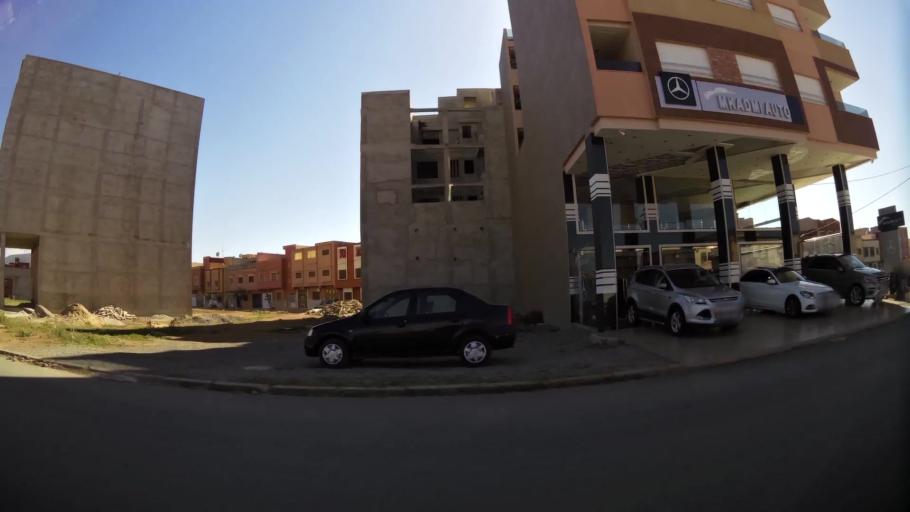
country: MA
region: Oriental
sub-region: Berkane-Taourirt
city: Berkane
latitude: 34.9404
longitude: -2.3348
